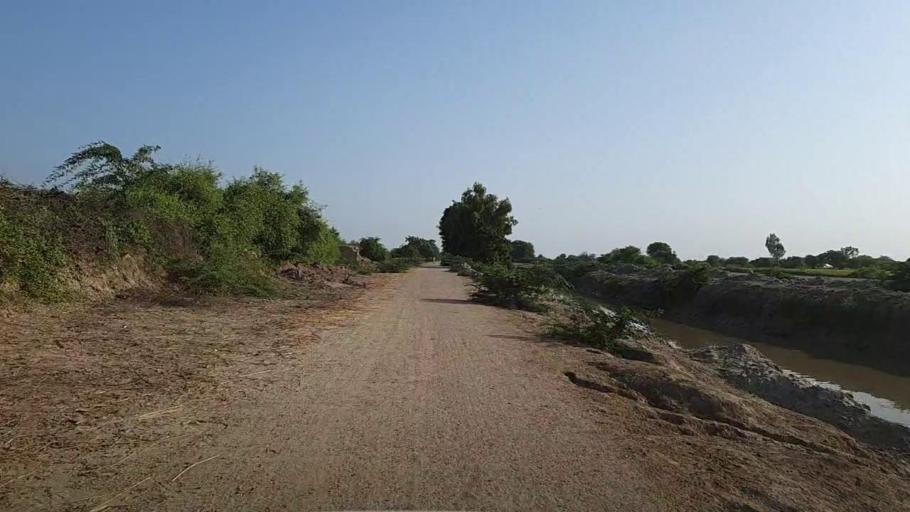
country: PK
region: Sindh
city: Kario
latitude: 24.7764
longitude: 68.6675
